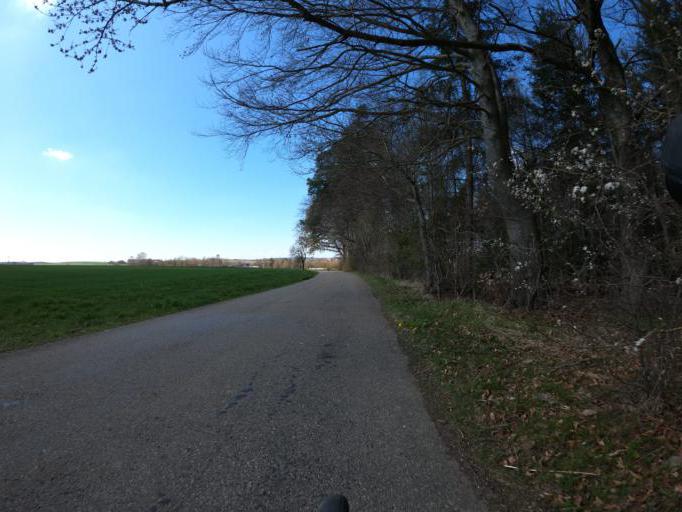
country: DE
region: Baden-Wuerttemberg
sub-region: Karlsruhe Region
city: Horb am Neckar
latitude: 48.4328
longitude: 8.7214
